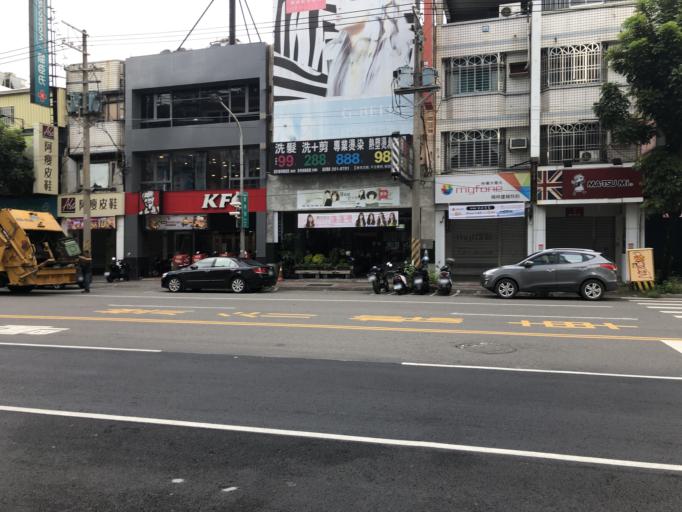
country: TW
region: Taiwan
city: Fengshan
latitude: 22.7269
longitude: 120.3269
